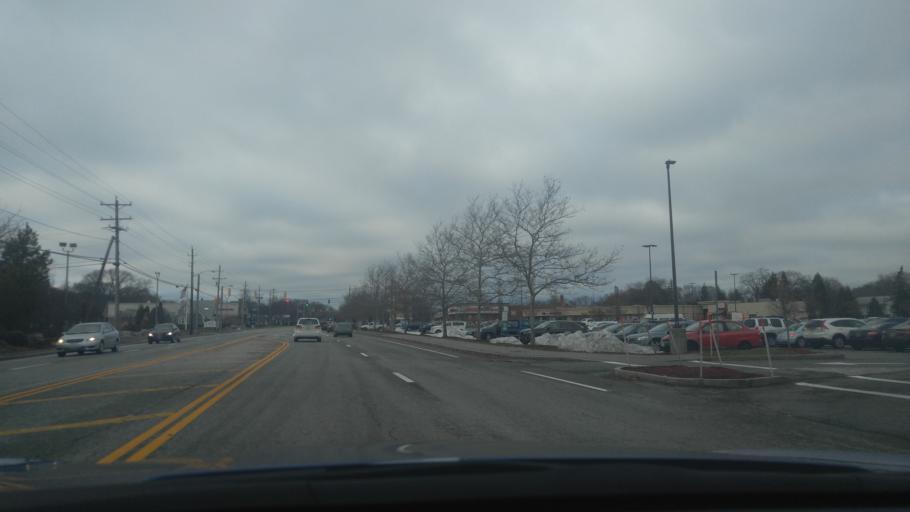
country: US
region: Rhode Island
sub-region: Kent County
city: Warwick
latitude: 41.7099
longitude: -71.3982
